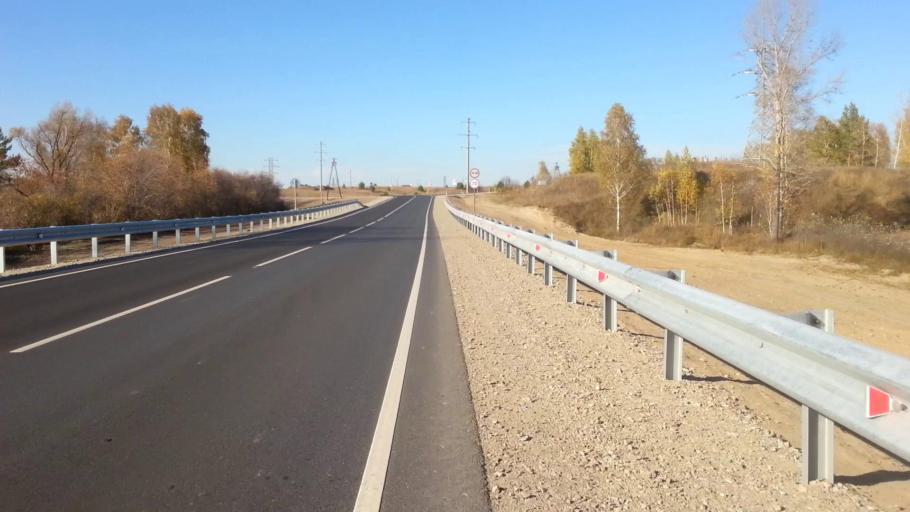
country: RU
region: Altai Krai
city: Sannikovo
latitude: 53.3268
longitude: 83.9417
